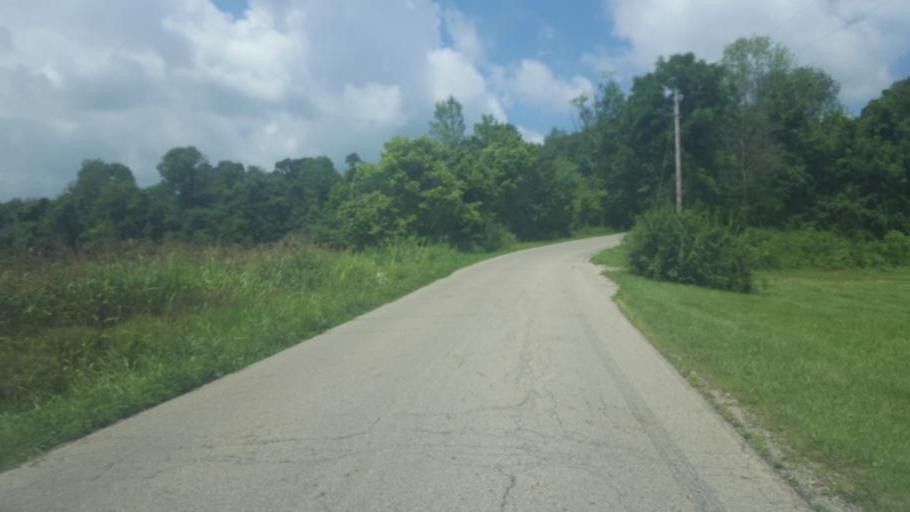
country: US
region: Ohio
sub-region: Ross County
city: Kingston
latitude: 39.4619
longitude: -82.7397
